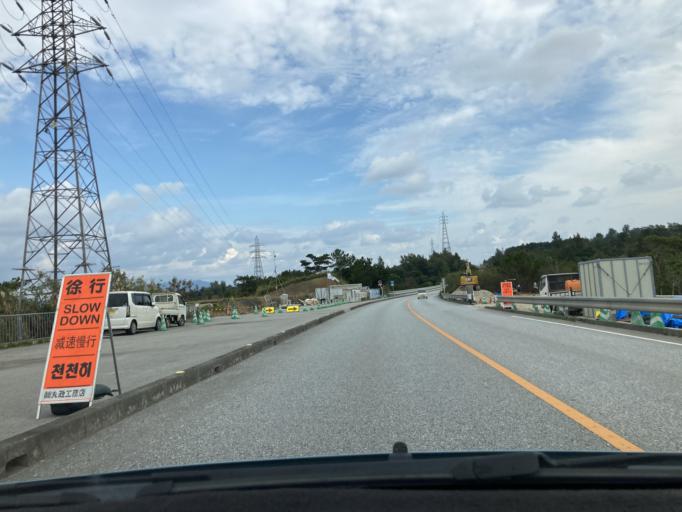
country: JP
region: Okinawa
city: Ishikawa
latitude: 26.4987
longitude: 127.8624
